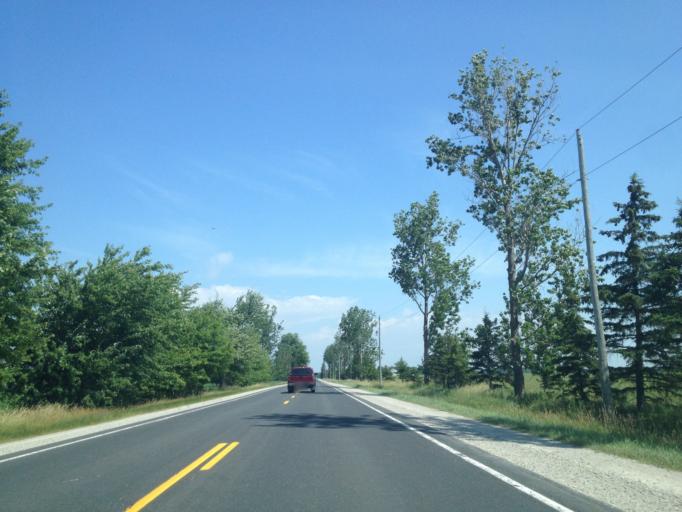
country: CA
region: Ontario
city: Huron East
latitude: 43.4155
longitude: -81.2216
